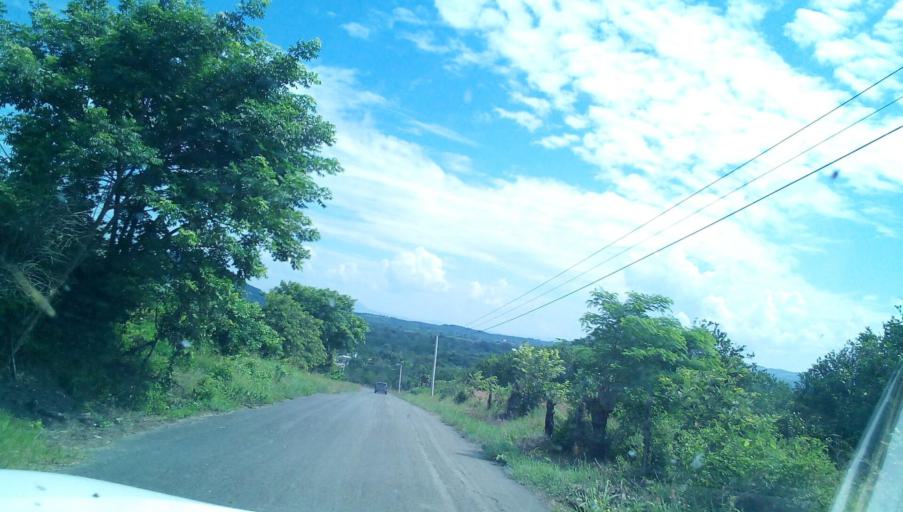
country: MX
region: Veracruz
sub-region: Alamo Temapache
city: Vegas de la Soledad y Soledad Dos
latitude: 20.8983
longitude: -97.9443
